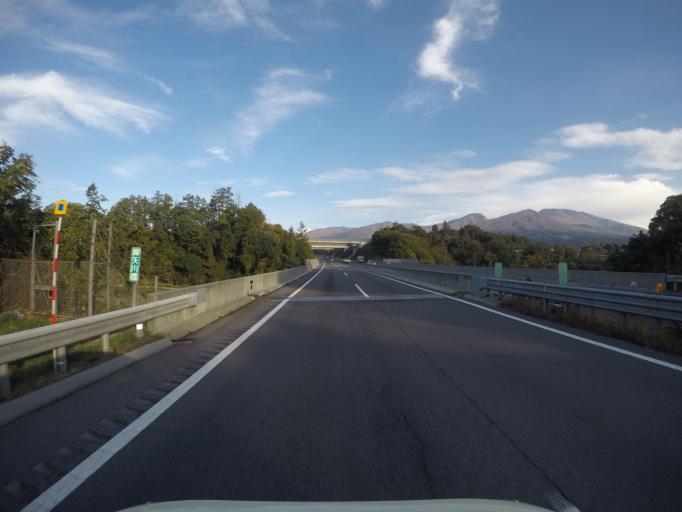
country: JP
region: Nagano
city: Komoro
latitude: 36.3164
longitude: 138.4787
